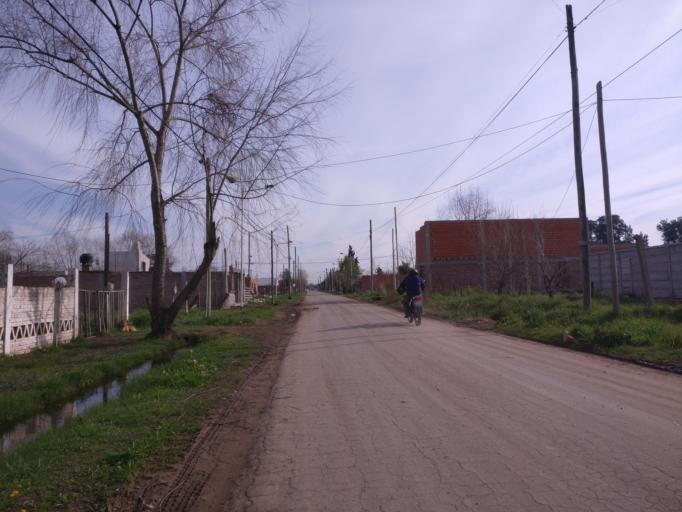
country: AR
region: Buenos Aires
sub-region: Partido de Ezeiza
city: Ezeiza
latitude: -34.9344
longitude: -58.6133
